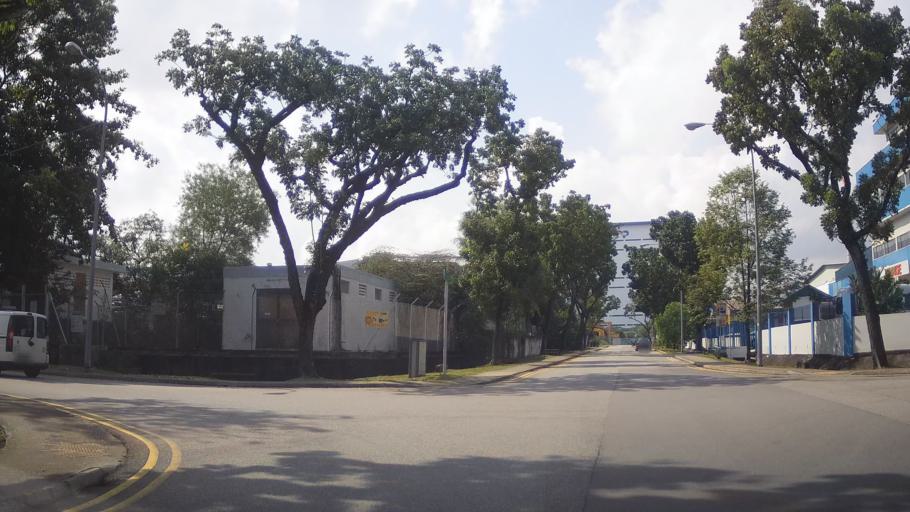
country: MY
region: Johor
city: Johor Bahru
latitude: 1.3266
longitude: 103.6993
